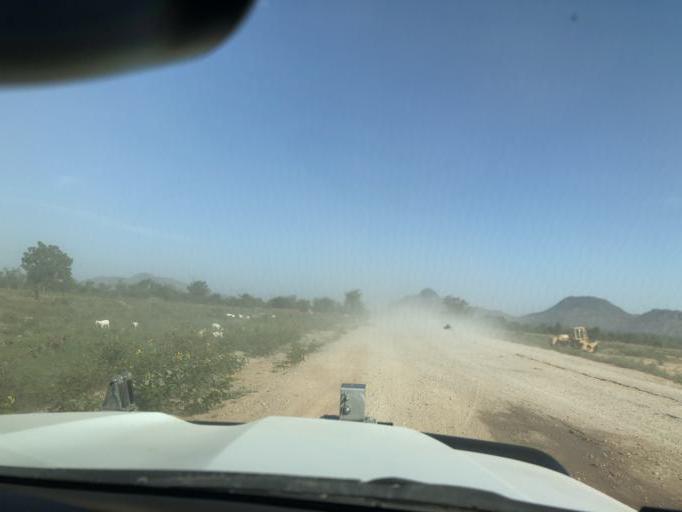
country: CM
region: Far North
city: Mora
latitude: 10.9252
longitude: 14.2156
